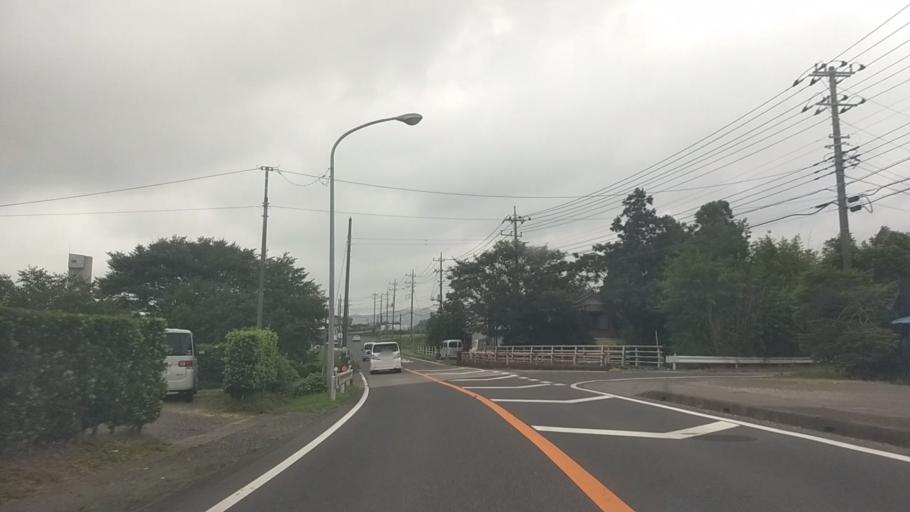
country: JP
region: Chiba
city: Kawaguchi
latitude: 35.1139
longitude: 140.0811
